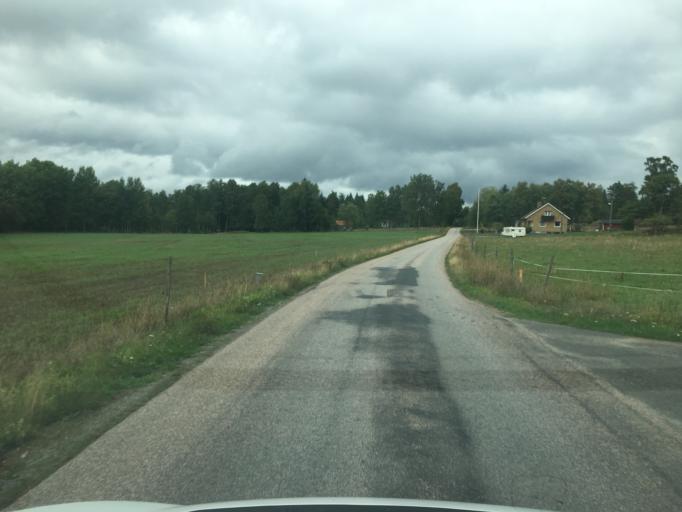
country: SE
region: Kronoberg
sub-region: Ljungby Kommun
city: Lagan
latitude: 56.9202
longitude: 14.0098
